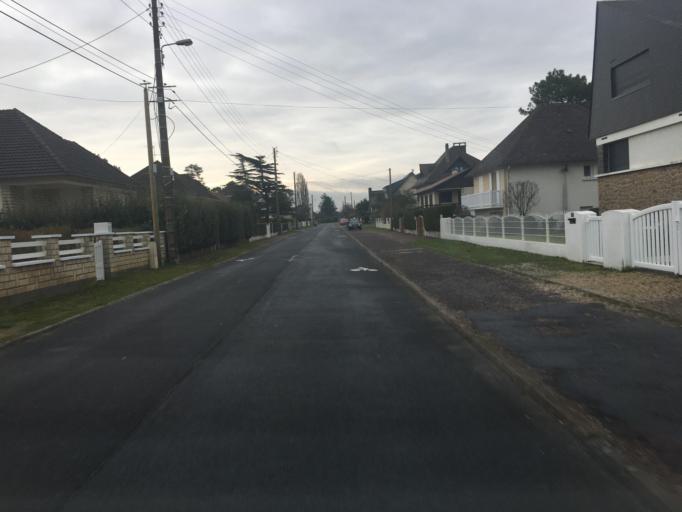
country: FR
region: Lower Normandy
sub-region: Departement du Calvados
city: Merville-Franceville-Plage
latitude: 49.2808
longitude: -0.2080
